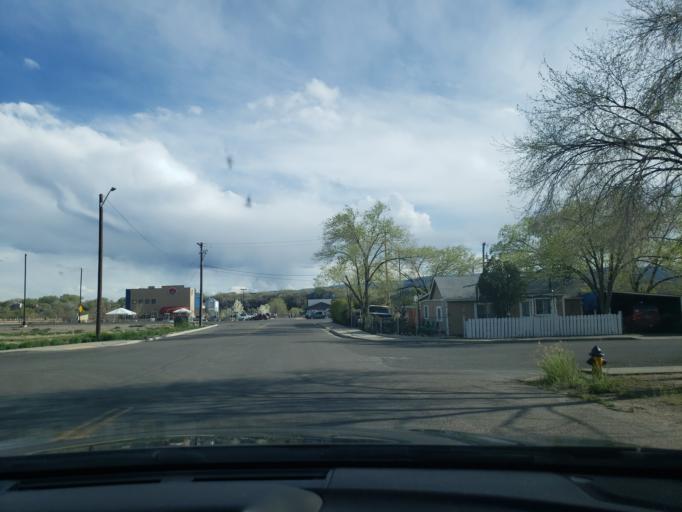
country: US
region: Colorado
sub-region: Mesa County
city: Grand Junction
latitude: 39.0568
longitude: -108.5577
